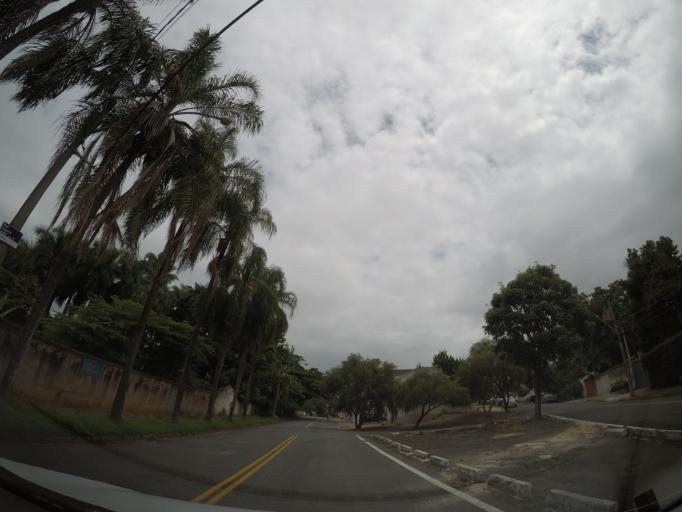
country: BR
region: Sao Paulo
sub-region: Campinas
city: Campinas
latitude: -22.9020
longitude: -47.0358
